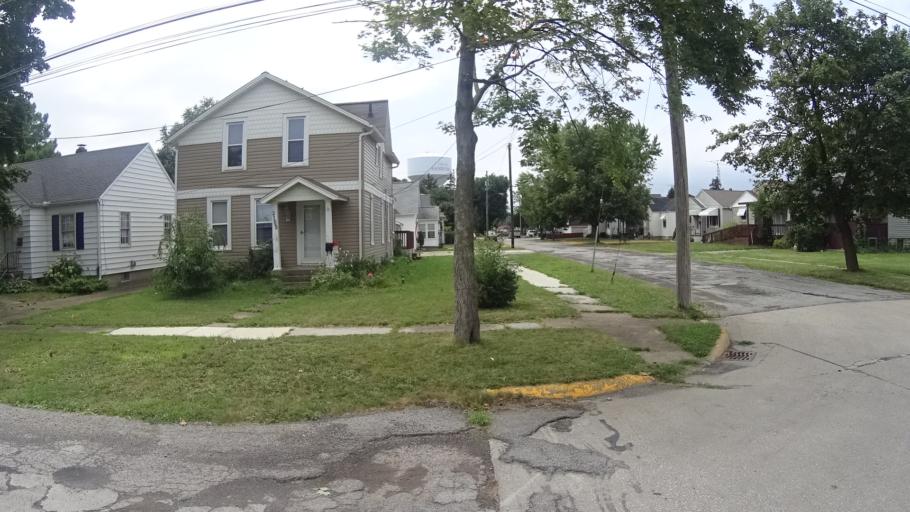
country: US
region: Ohio
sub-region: Erie County
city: Sandusky
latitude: 41.4378
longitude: -82.6989
